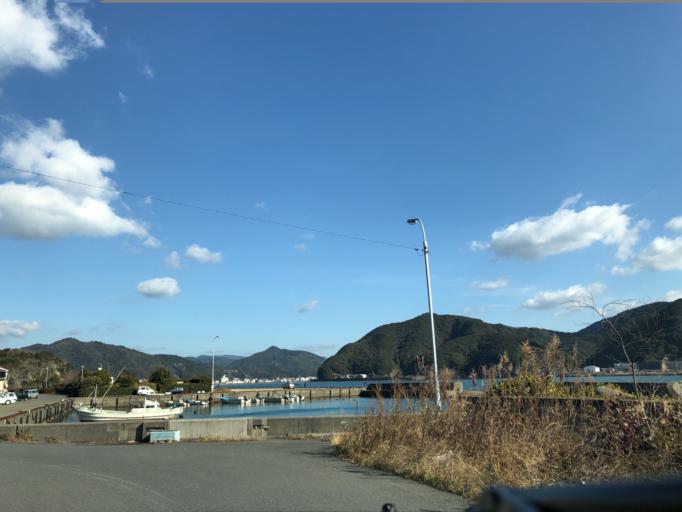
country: JP
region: Kochi
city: Sukumo
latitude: 32.9142
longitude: 132.7042
